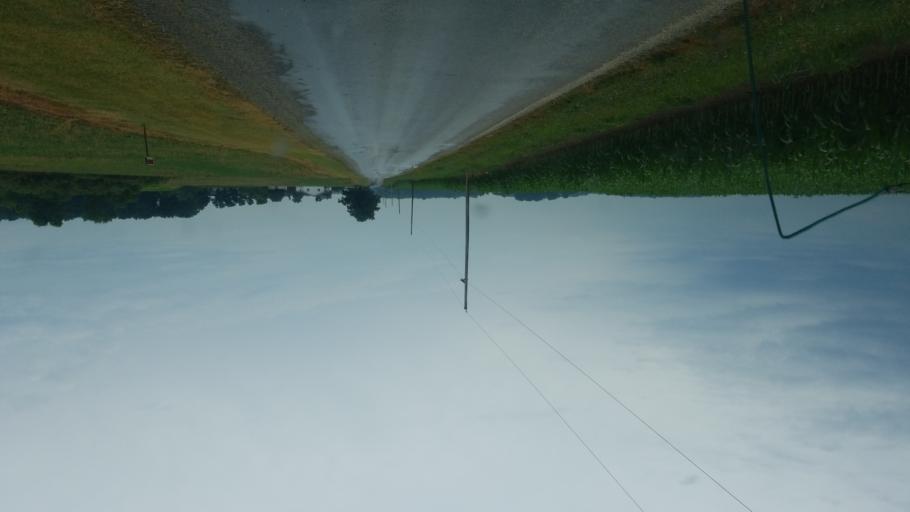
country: US
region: Ohio
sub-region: Williams County
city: Edgerton
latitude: 41.4221
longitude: -84.6704
